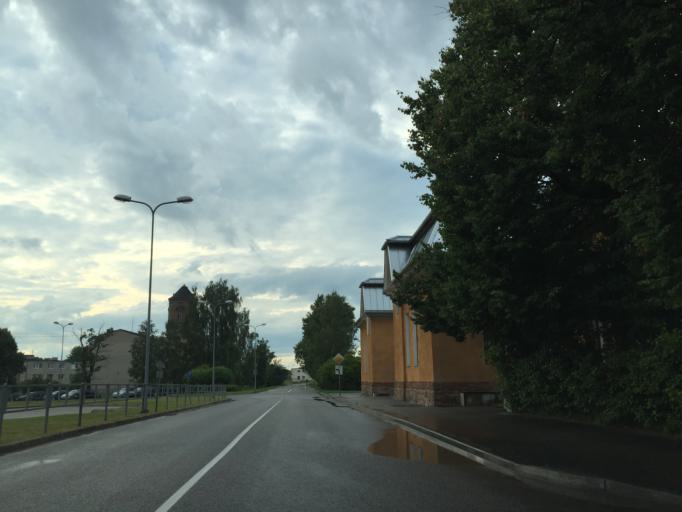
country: LV
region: Dobeles Rajons
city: Dobele
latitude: 56.6283
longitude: 23.2849
